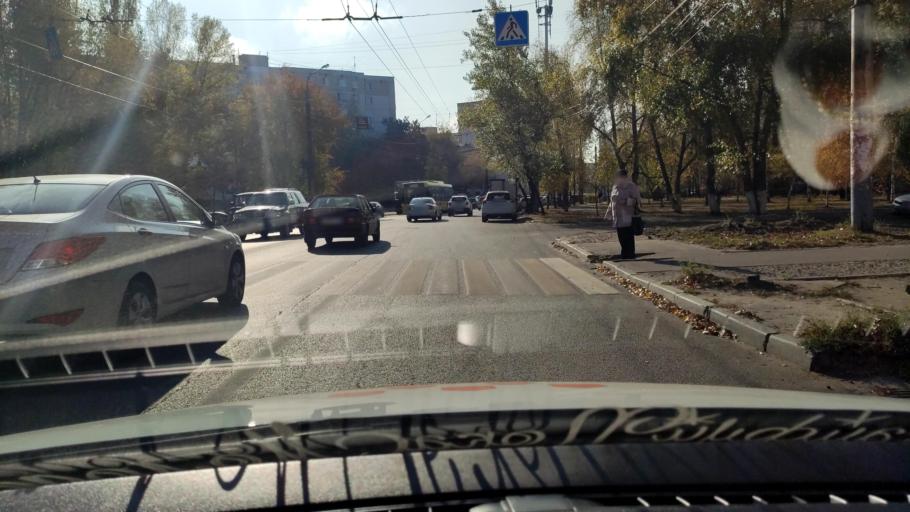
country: RU
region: Voronezj
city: Podgornoye
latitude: 51.7106
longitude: 39.1516
